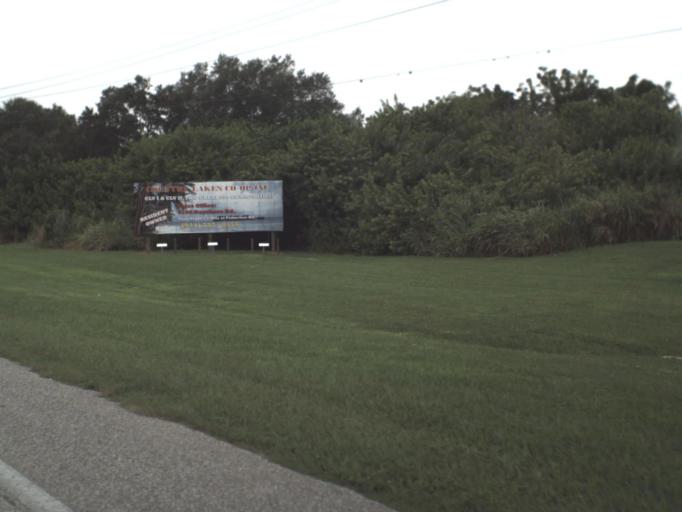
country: US
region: Florida
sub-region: Manatee County
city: Memphis
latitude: 27.5725
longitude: -82.5423
